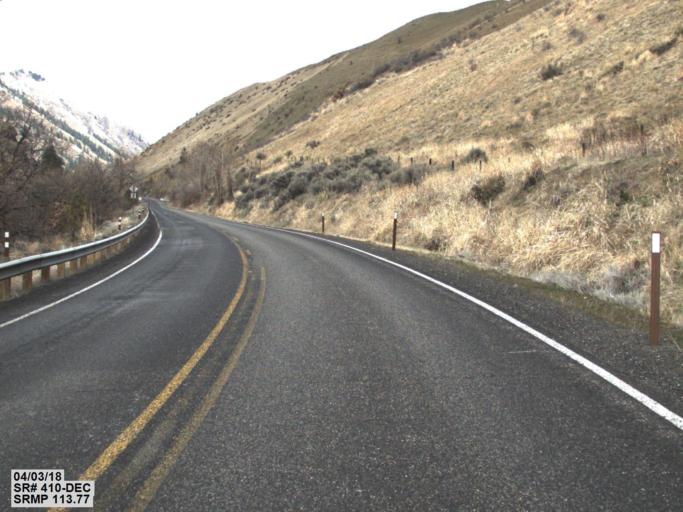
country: US
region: Washington
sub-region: Yakima County
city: Tieton
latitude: 46.7648
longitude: -120.8283
